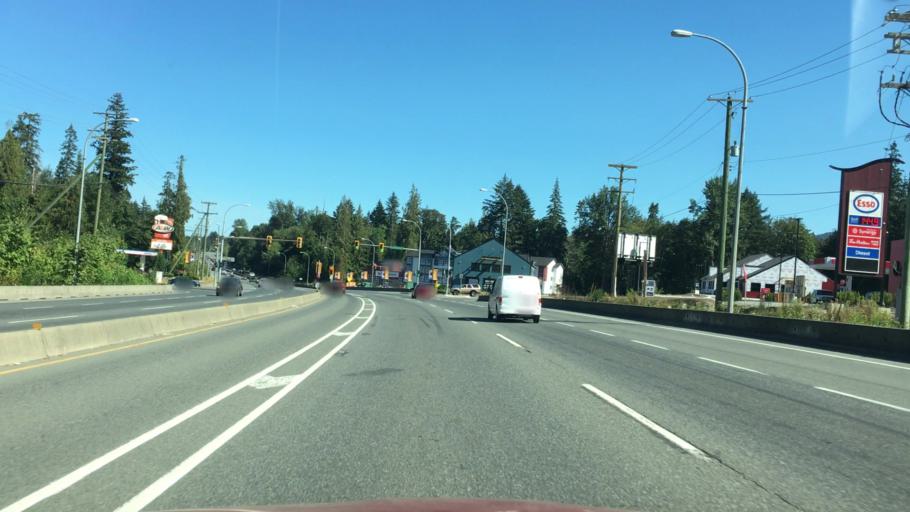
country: CA
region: British Columbia
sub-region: Cowichan Valley Regional District
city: Ladysmith
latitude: 49.0159
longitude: -123.8556
